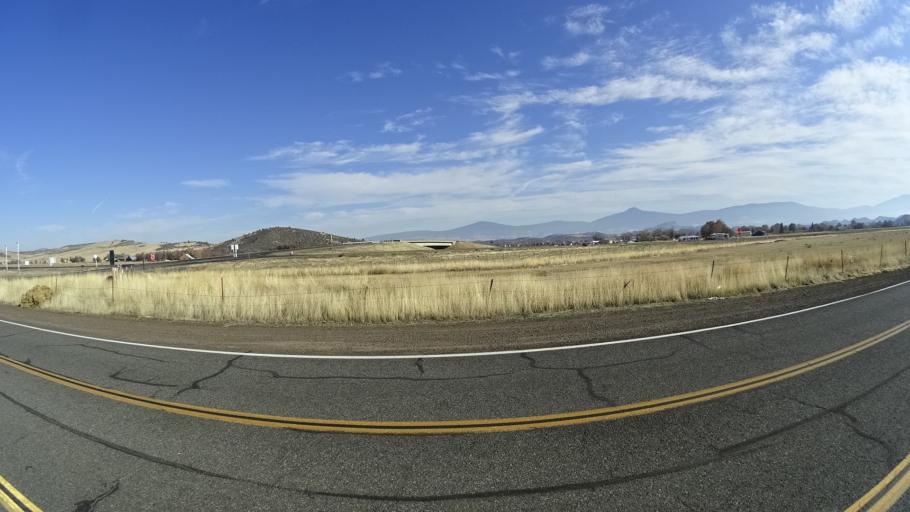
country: US
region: California
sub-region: Siskiyou County
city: Montague
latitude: 41.6447
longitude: -122.5372
